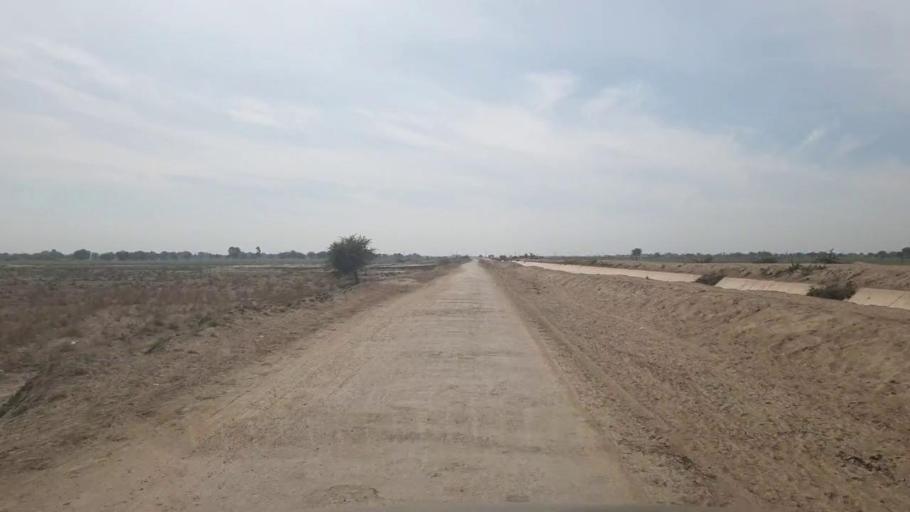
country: PK
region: Sindh
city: Umarkot
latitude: 25.3333
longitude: 69.6037
